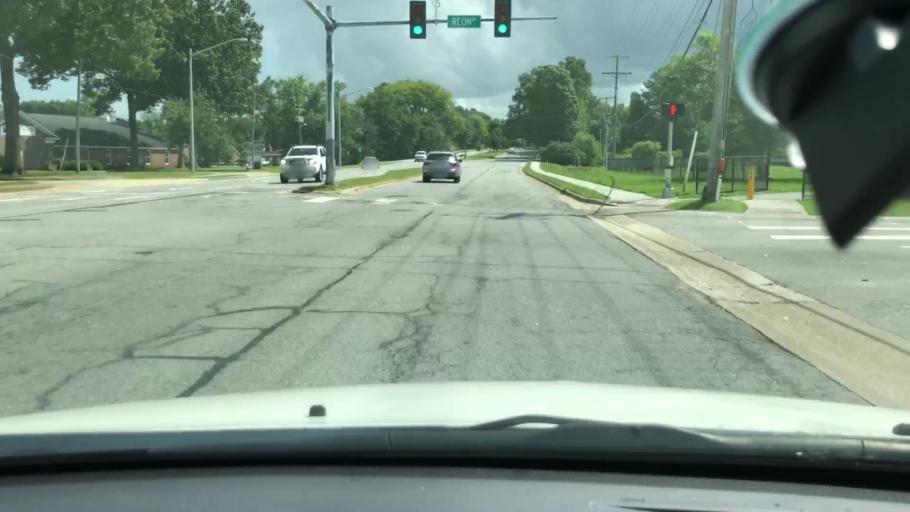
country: US
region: Virginia
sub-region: City of Chesapeake
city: Chesapeake
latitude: 36.8127
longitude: -76.1995
